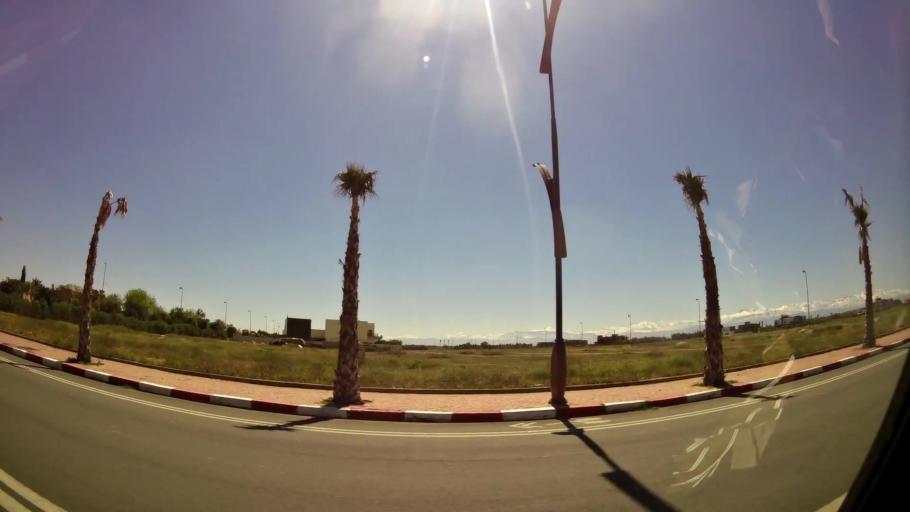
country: MA
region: Marrakech-Tensift-Al Haouz
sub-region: Marrakech
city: Marrakesh
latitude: 31.5978
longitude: -8.0029
